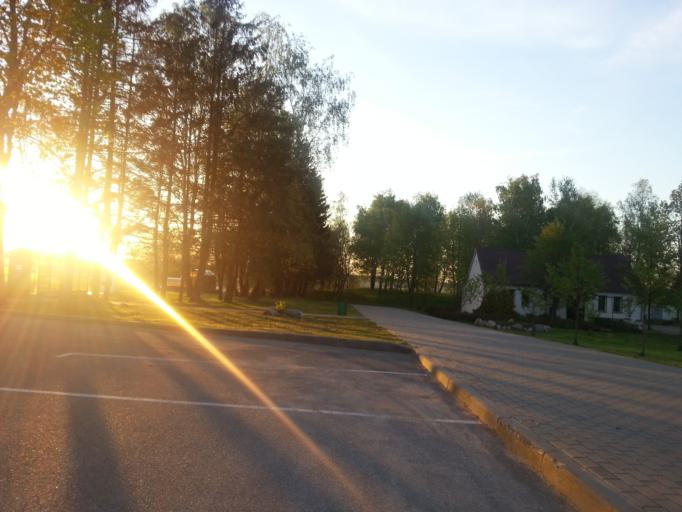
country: BY
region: Minsk
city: Slabada
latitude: 54.0191
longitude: 27.8922
